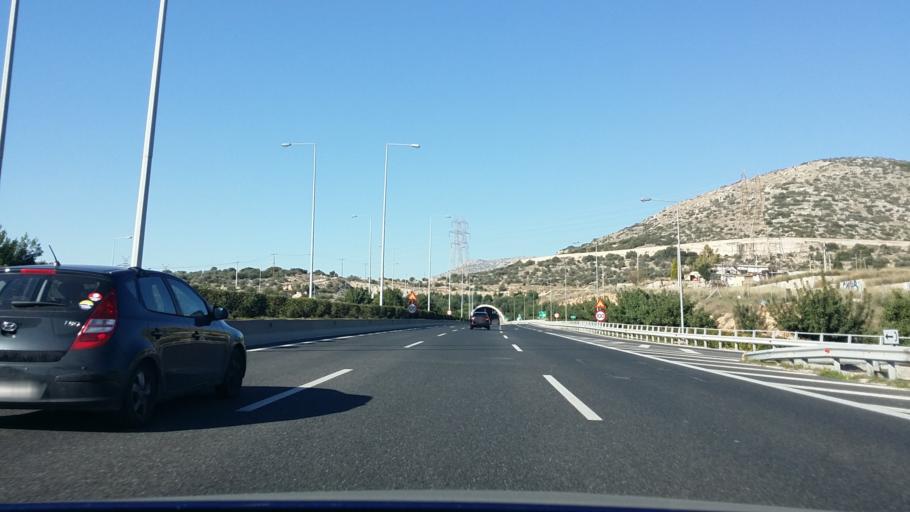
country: GR
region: Attica
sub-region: Nomarchia Dytikis Attikis
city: Ano Liosia
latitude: 38.0793
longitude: 23.6767
